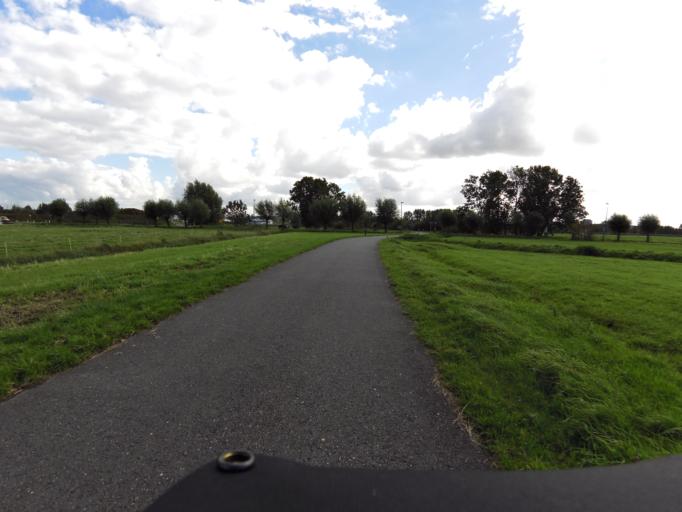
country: NL
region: South Holland
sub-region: Gemeente Vlaardingen
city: Vlaardingen
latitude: 51.9475
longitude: 4.3523
